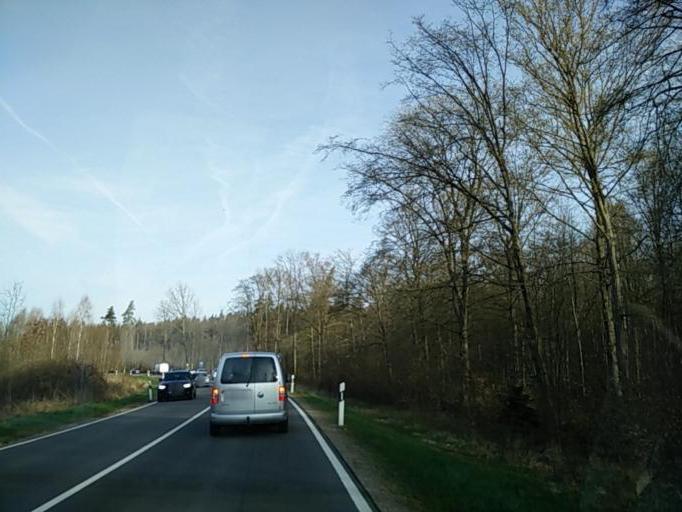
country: DE
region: Baden-Wuerttemberg
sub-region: Regierungsbezirk Stuttgart
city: Weil im Schonbuch
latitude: 48.6083
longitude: 9.0481
